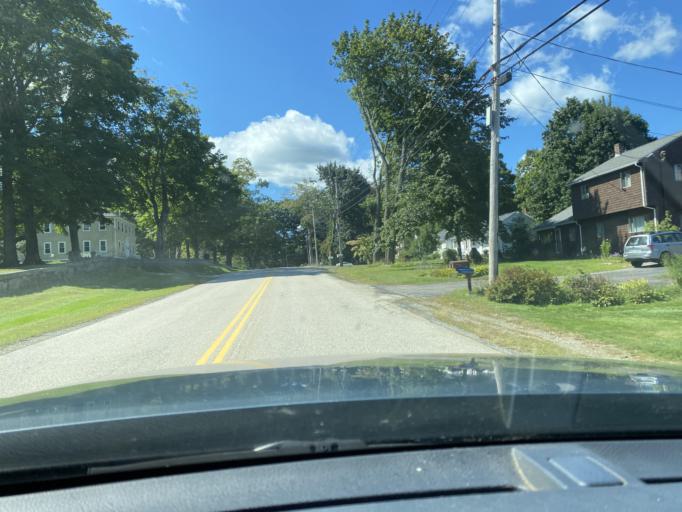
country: US
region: New Hampshire
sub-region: Rockingham County
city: Greenland
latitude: 43.0517
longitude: -70.8191
